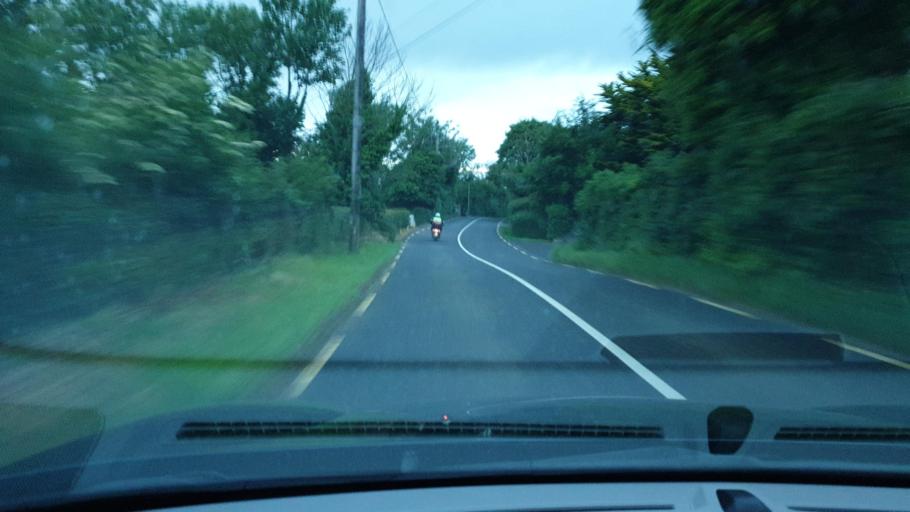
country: IE
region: Leinster
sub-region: An Mhi
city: Ashbourne
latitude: 53.5128
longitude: -6.3192
